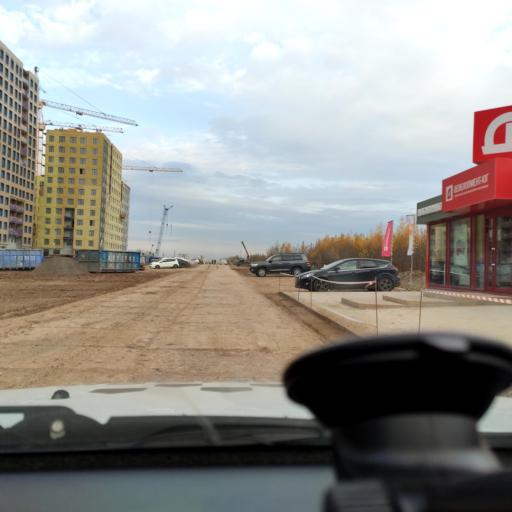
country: RU
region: Perm
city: Perm
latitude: 58.0103
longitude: 56.3331
